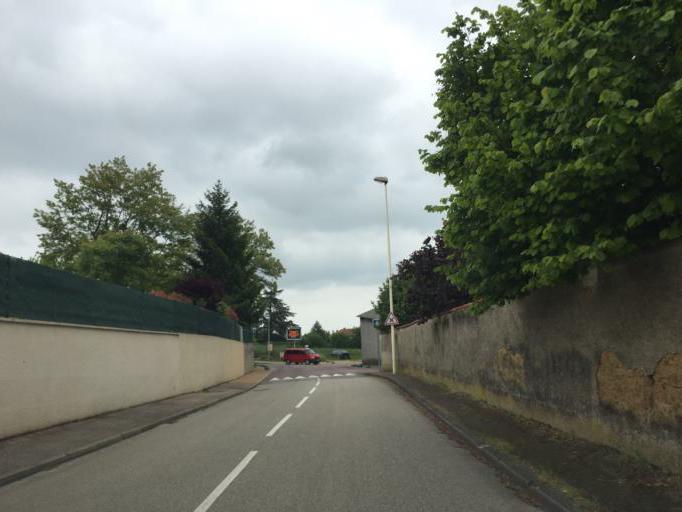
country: FR
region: Rhone-Alpes
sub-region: Departement de l'Ain
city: Miribel
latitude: 45.8209
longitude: 4.9288
